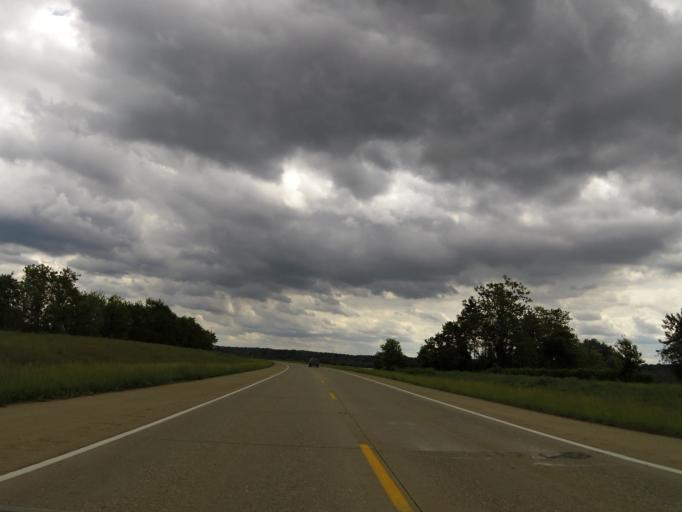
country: US
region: West Virginia
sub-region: Jackson County
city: Ravenswood
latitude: 38.9380
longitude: -81.7883
